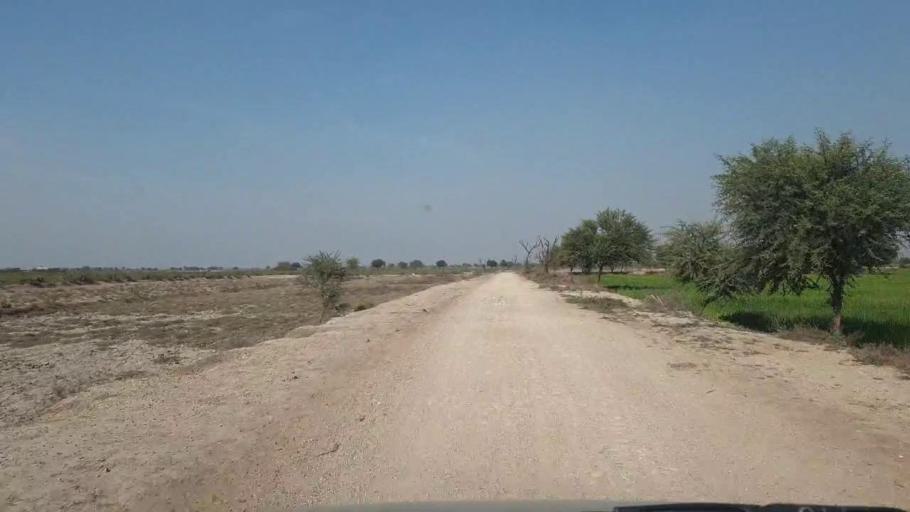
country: PK
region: Sindh
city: Chambar
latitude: 25.3289
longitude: 68.8098
